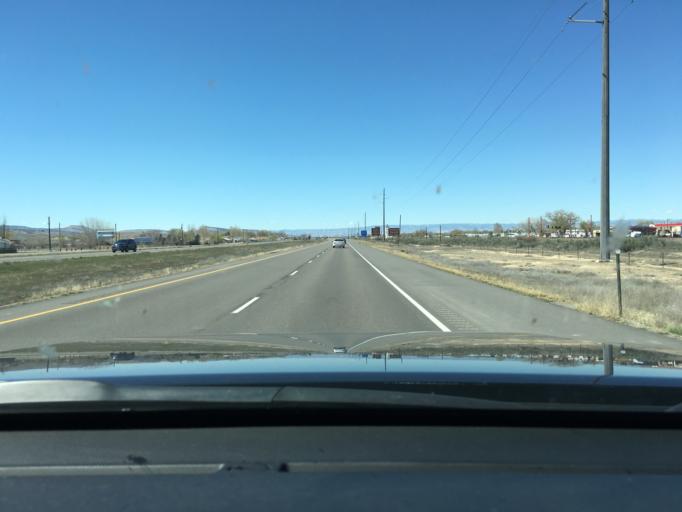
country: US
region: Colorado
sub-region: Mesa County
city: Fruita
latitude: 39.1462
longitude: -108.7175
